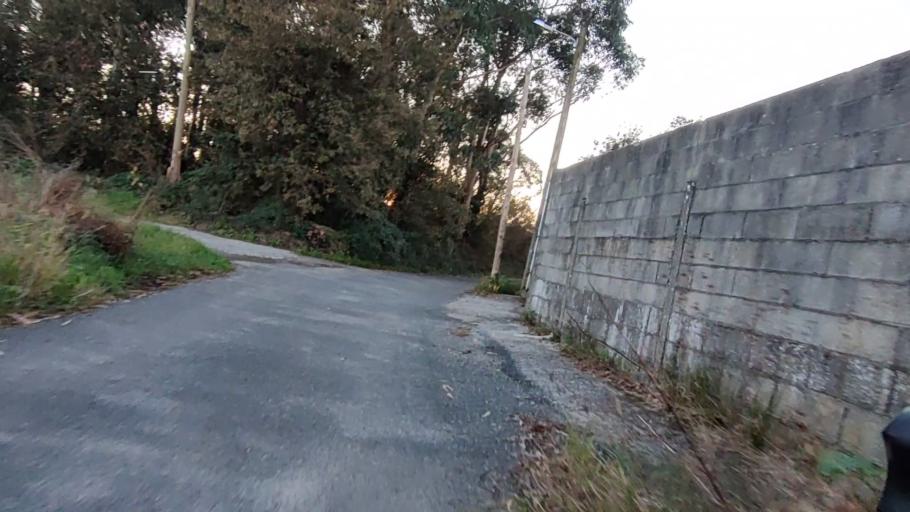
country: ES
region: Galicia
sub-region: Provincia da Coruna
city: Boiro
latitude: 42.6394
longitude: -8.8761
